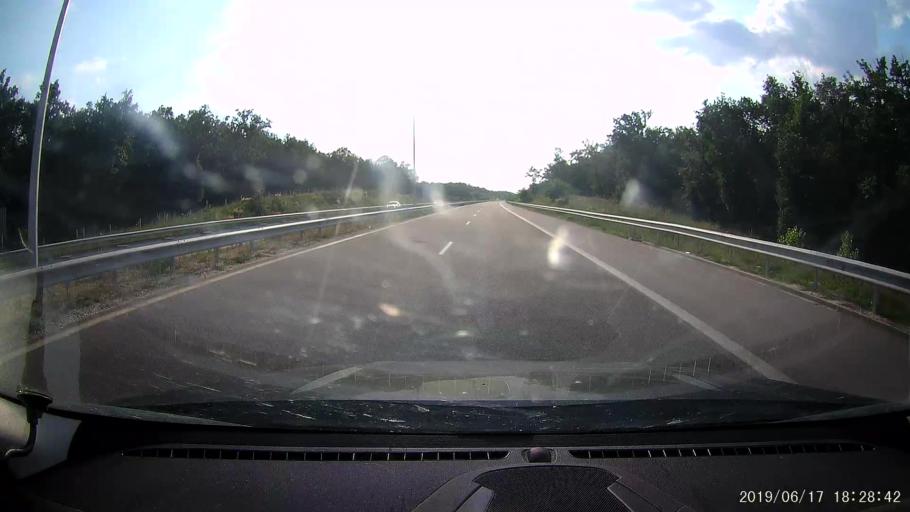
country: BG
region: Khaskovo
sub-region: Obshtina Dimitrovgrad
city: Dimitrovgrad
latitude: 42.0241
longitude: 25.5727
